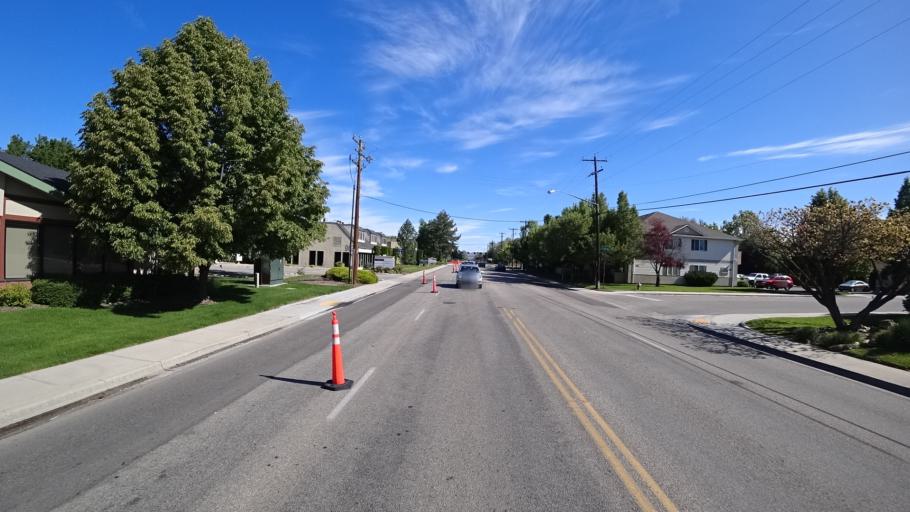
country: US
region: Idaho
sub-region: Ada County
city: Garden City
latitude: 43.5951
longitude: -116.2437
